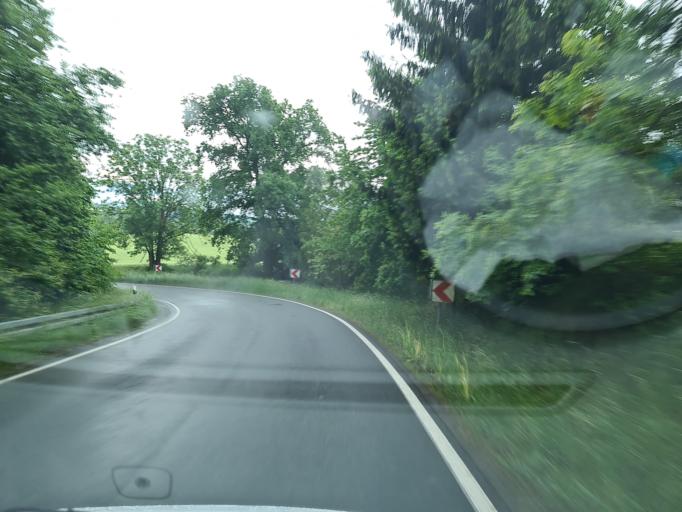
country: DE
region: Thuringia
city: Tanna
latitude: 50.5086
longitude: 11.8964
